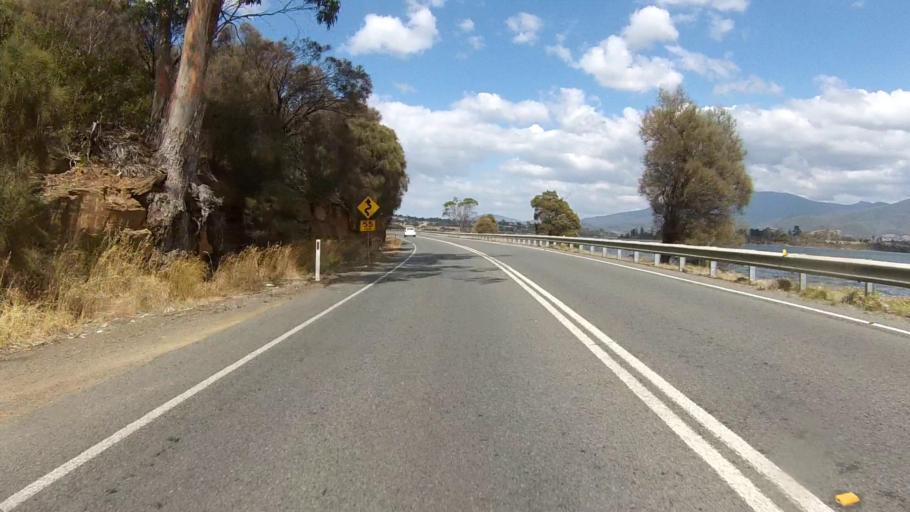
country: AU
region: Tasmania
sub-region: Brighton
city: Old Beach
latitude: -42.7809
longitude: 147.2854
